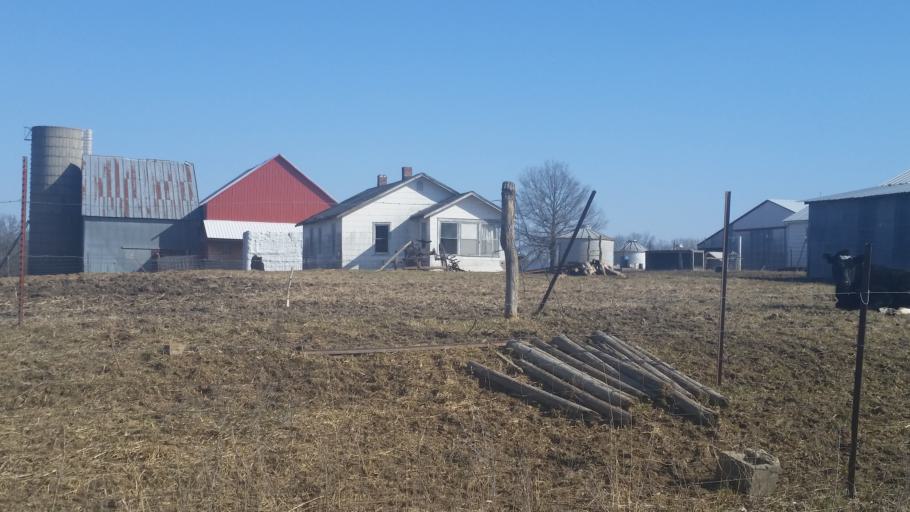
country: US
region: Missouri
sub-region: Randolph County
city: Moberly
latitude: 39.3254
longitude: -92.3035
